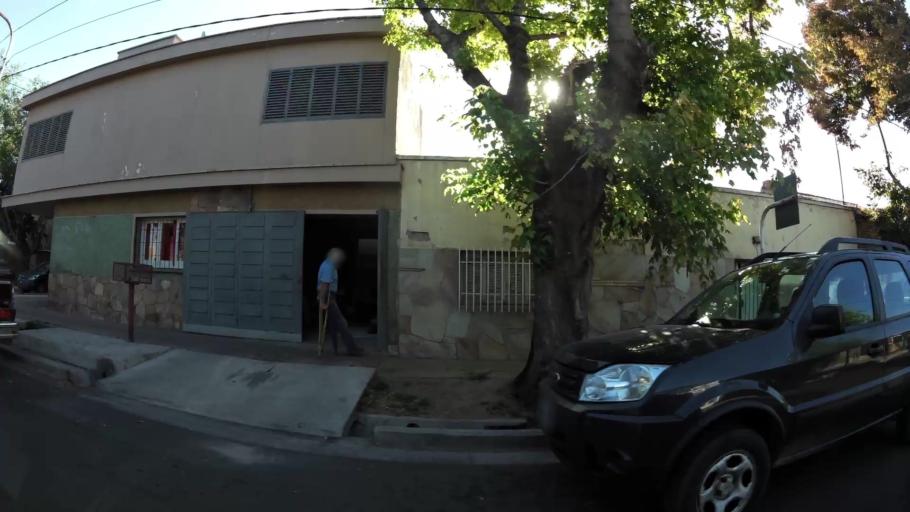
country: AR
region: Mendoza
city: Mendoza
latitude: -32.9017
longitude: -68.8352
